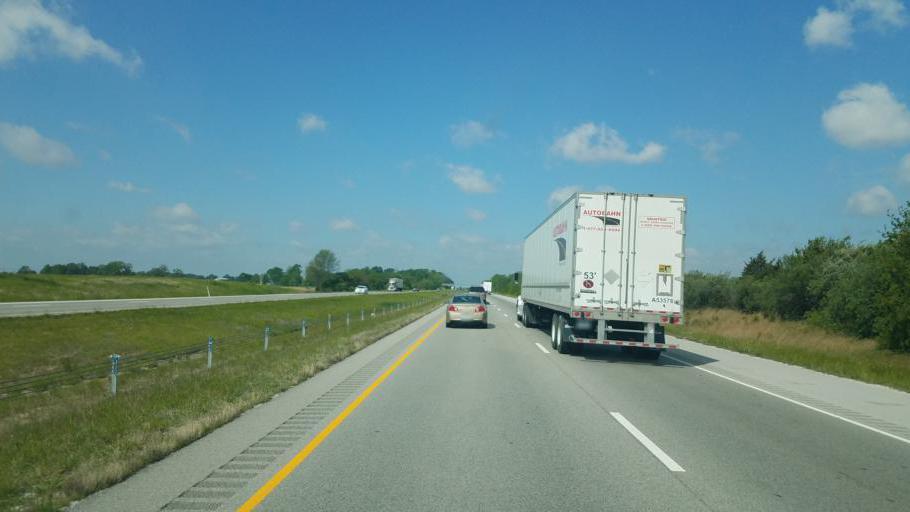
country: US
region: Indiana
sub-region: Morgan County
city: Monrovia
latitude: 39.5894
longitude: -86.5594
